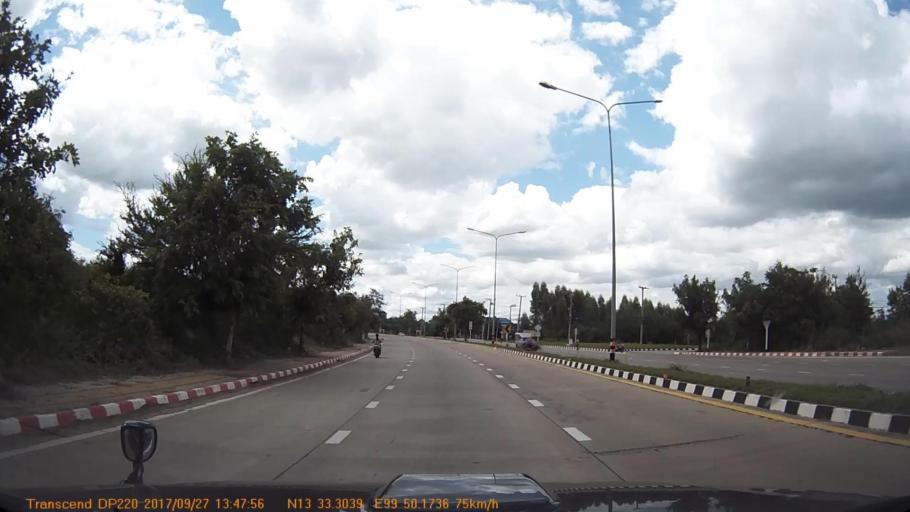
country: TH
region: Ratchaburi
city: Ratchaburi
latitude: 13.5550
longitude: 99.8363
